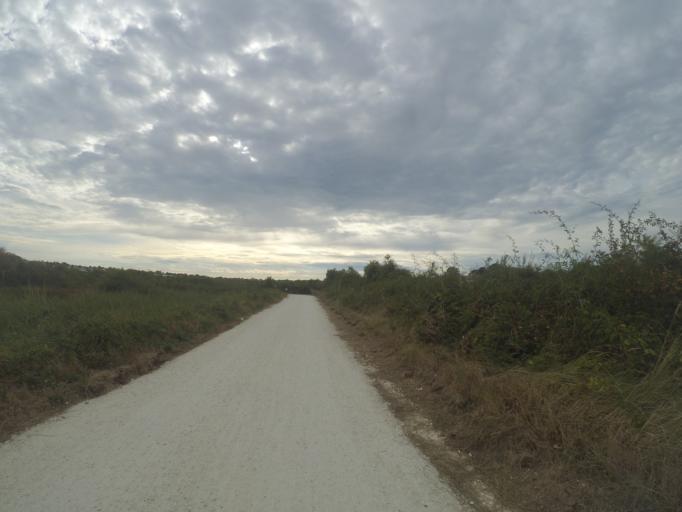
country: FR
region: Poitou-Charentes
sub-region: Departement de la Charente-Maritime
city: Meschers-sur-Gironde
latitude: 45.5579
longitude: -0.9381
